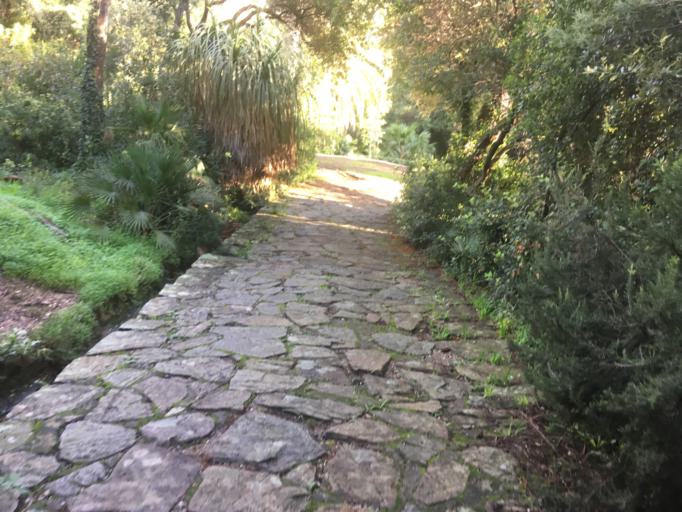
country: FR
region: Provence-Alpes-Cote d'Azur
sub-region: Departement du Var
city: Cavalaire-sur-Mer
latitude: 43.1549
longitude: 6.4825
